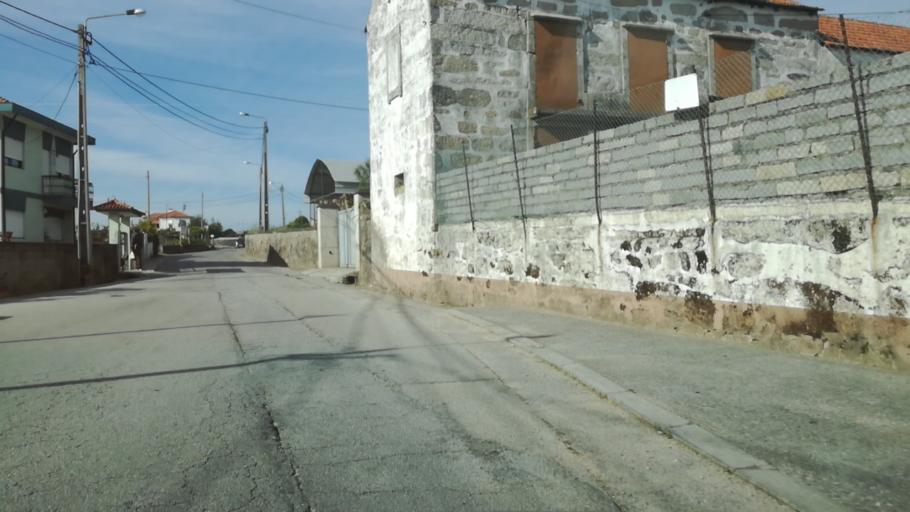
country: PT
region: Porto
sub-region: Maia
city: Nogueira
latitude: 41.2386
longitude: -8.5925
